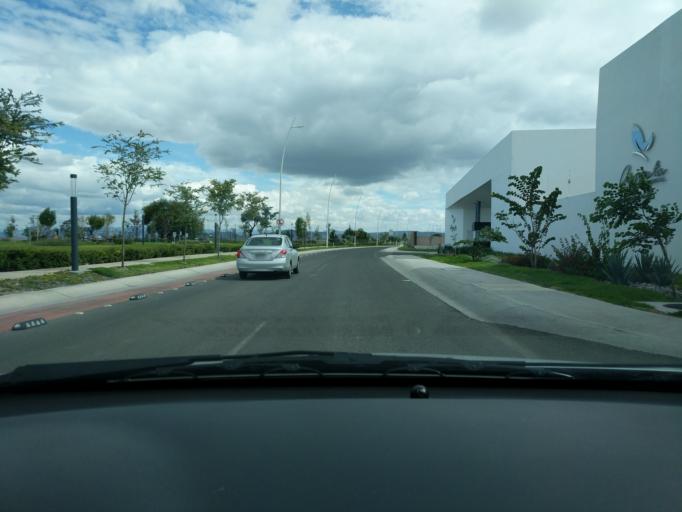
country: MX
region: Queretaro
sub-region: El Marques
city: La Pradera
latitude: 20.6610
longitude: -100.3130
